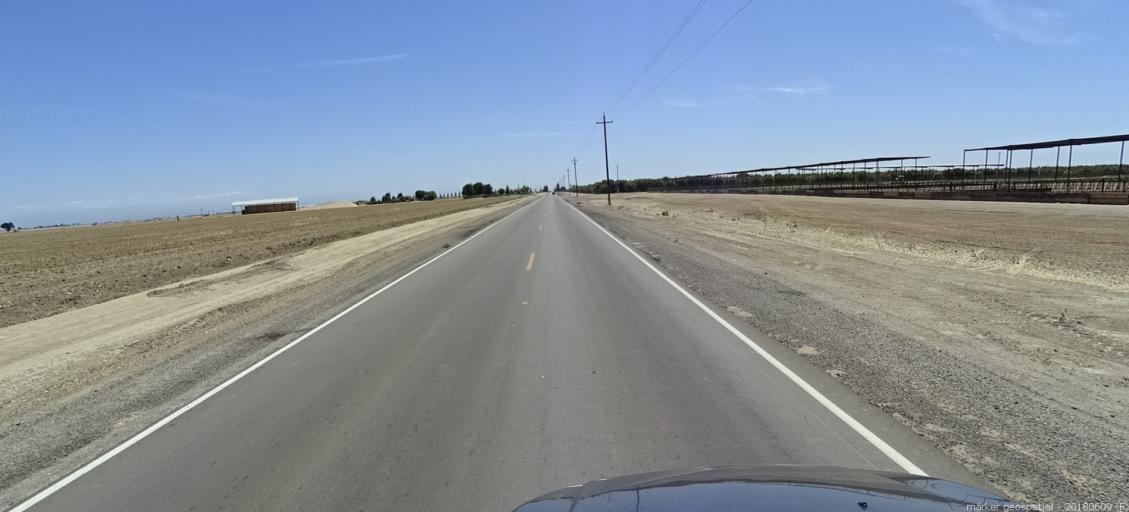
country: US
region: California
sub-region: Madera County
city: Fairmead
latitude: 36.9527
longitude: -120.3064
